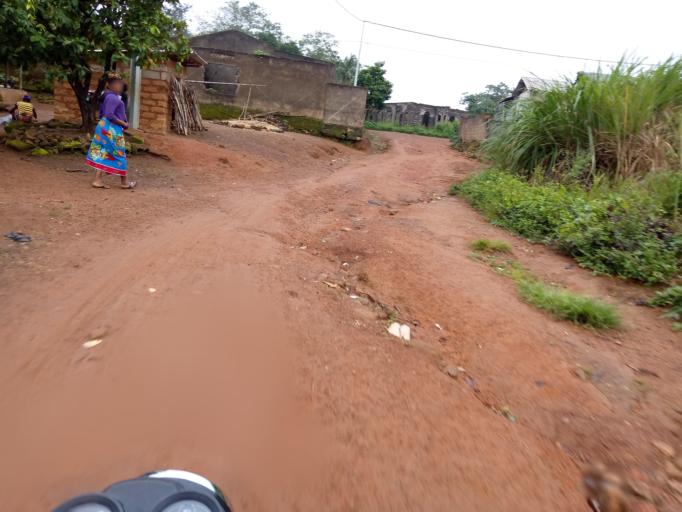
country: SL
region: Eastern Province
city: Buedu
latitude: 8.4634
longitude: -10.3402
